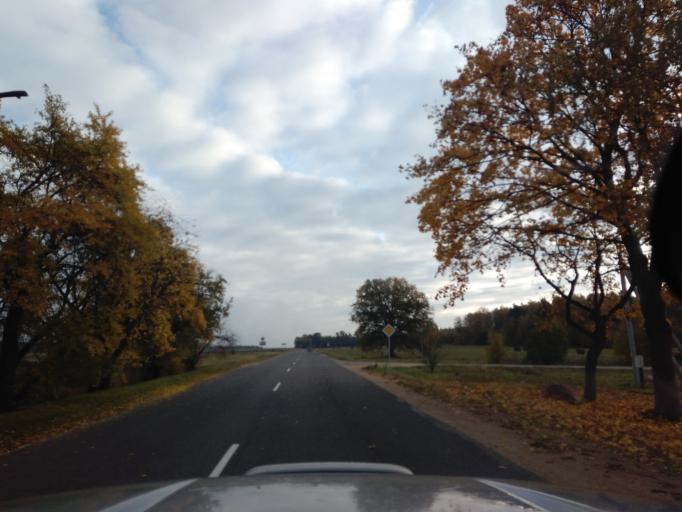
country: BY
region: Minsk
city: Kapyl'
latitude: 53.1636
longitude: 27.1017
